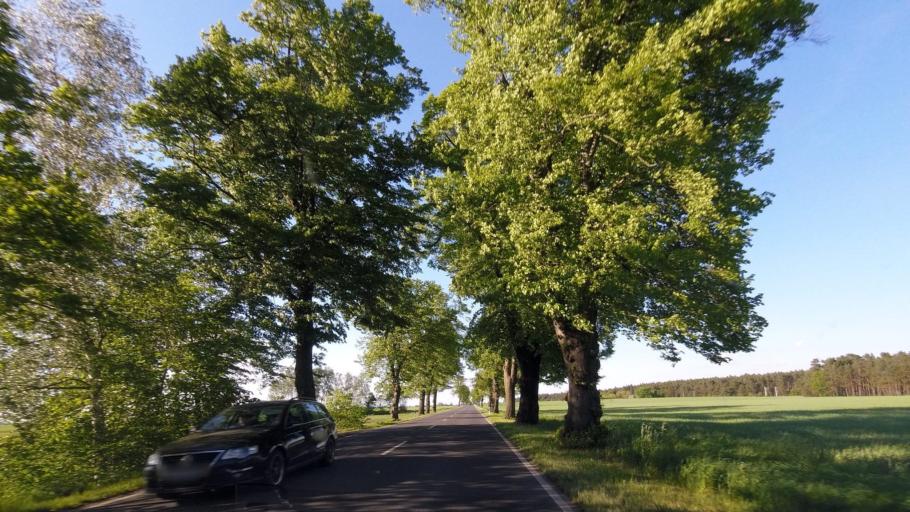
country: DE
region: Brandenburg
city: Luebben
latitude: 51.9112
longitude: 13.8947
